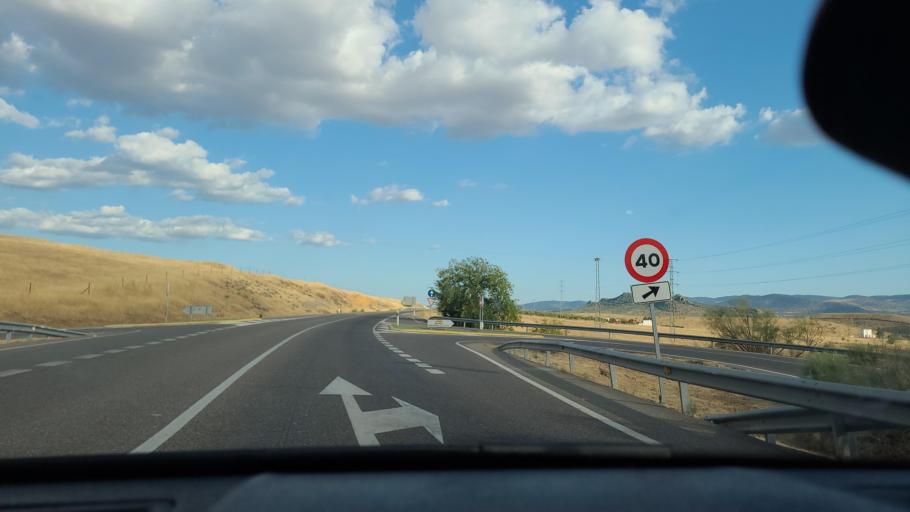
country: ES
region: Andalusia
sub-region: Province of Cordoba
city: Belmez
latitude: 38.2778
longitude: -5.2016
